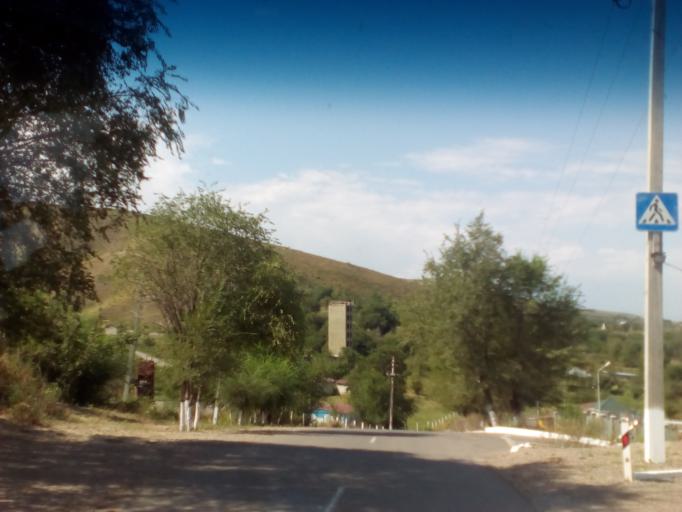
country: KZ
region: Almaty Oblysy
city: Burunday
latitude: 43.1533
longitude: 76.3799
